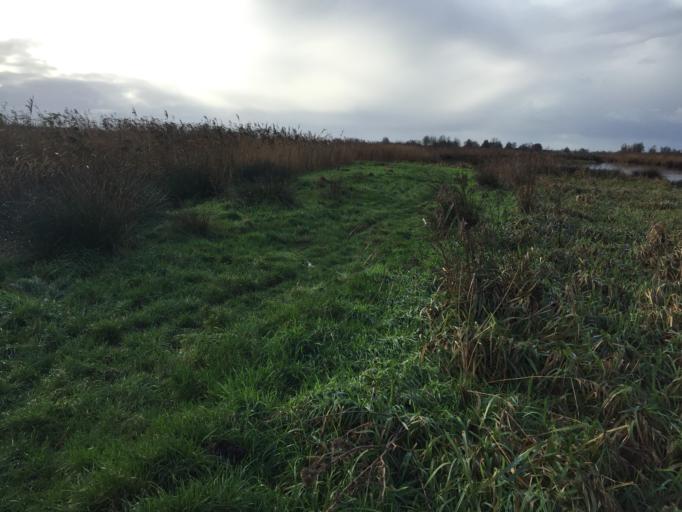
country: NL
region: Utrecht
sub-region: Gemeente De Ronde Venen
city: Mijdrecht
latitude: 52.1788
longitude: 4.8265
